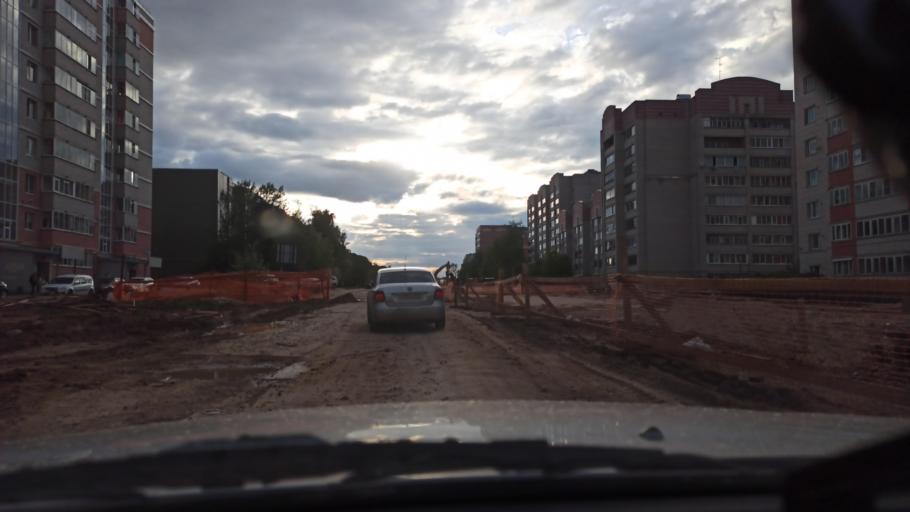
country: RU
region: Vologda
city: Vologda
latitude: 59.1950
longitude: 39.8775
